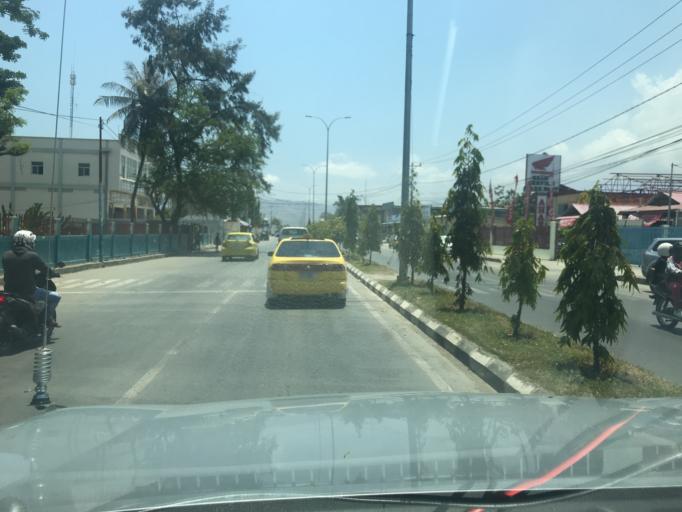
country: TL
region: Dili
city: Dili
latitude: -8.5542
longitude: 125.5462
